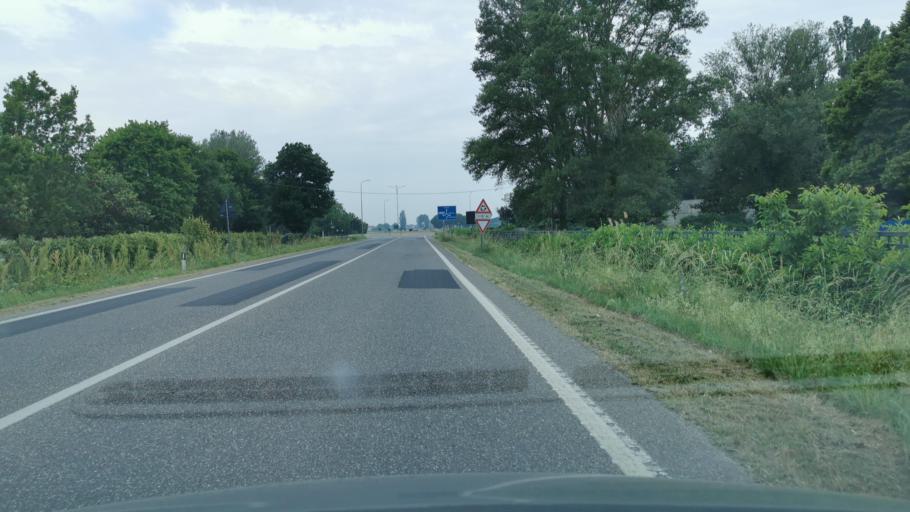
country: IT
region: Emilia-Romagna
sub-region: Provincia di Ravenna
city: Godo
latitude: 44.3949
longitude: 12.0702
